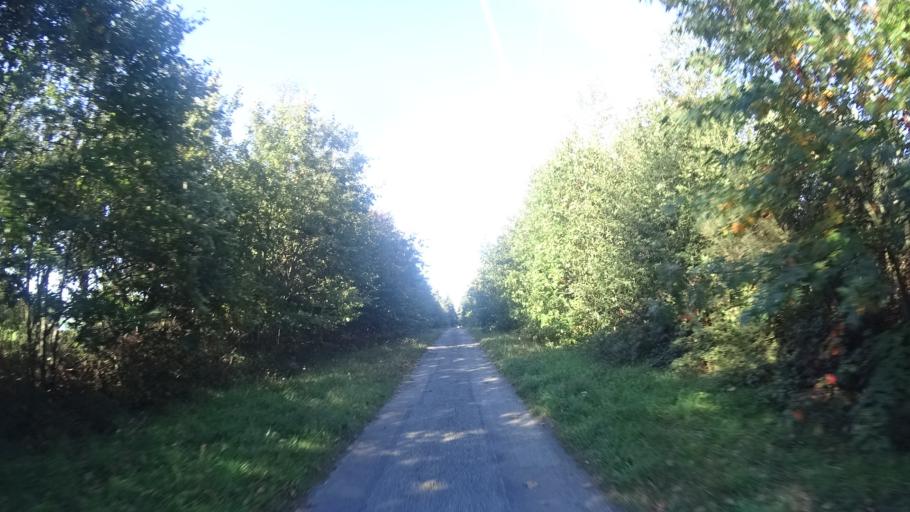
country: FR
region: Brittany
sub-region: Departement du Morbihan
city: Peillac
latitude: 47.7089
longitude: -2.1858
